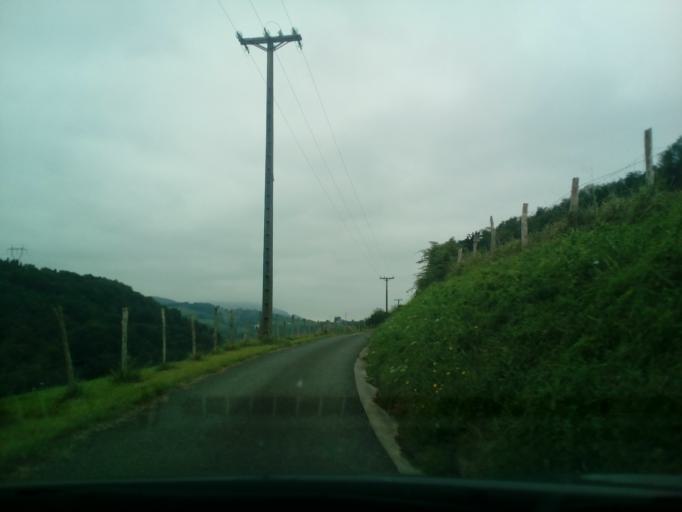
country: ES
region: Basque Country
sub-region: Provincia de Guipuzcoa
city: Andoain
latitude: 43.2159
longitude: -2.0084
